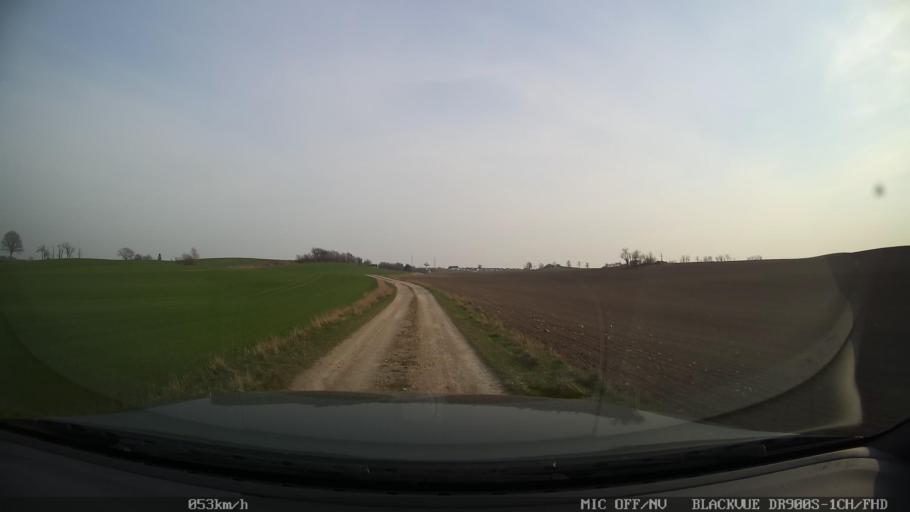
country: SE
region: Skane
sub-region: Ystads Kommun
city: Ystad
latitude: 55.4568
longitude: 13.7911
